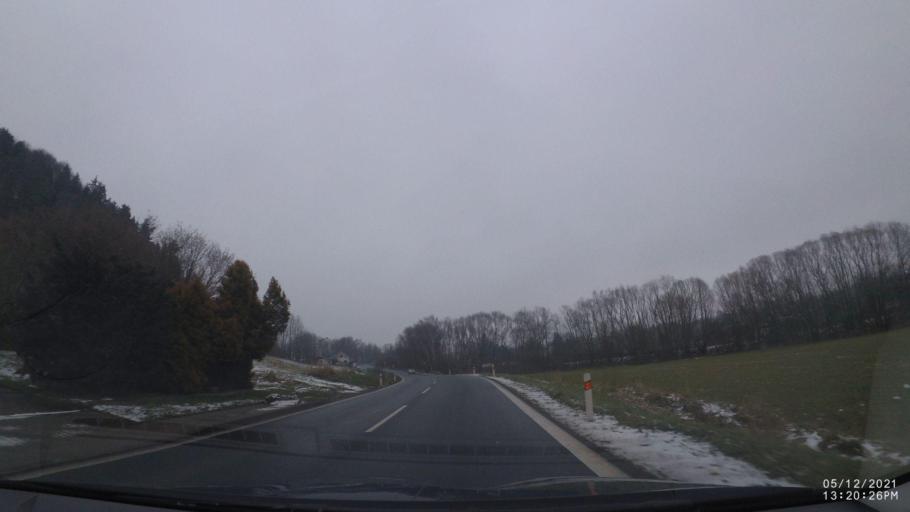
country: CZ
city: Velke Porici
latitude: 50.4501
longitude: 16.1885
